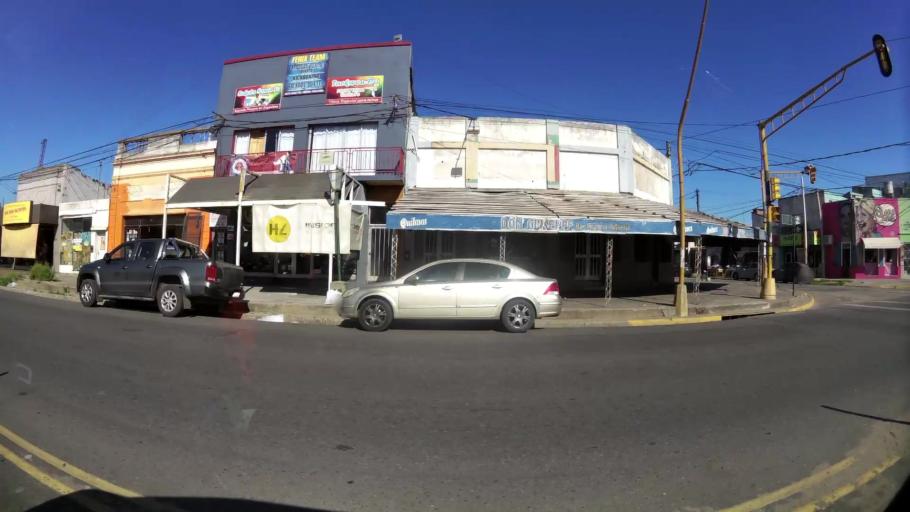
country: AR
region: Santa Fe
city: Santa Fe de la Vera Cruz
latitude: -31.6102
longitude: -60.6943
